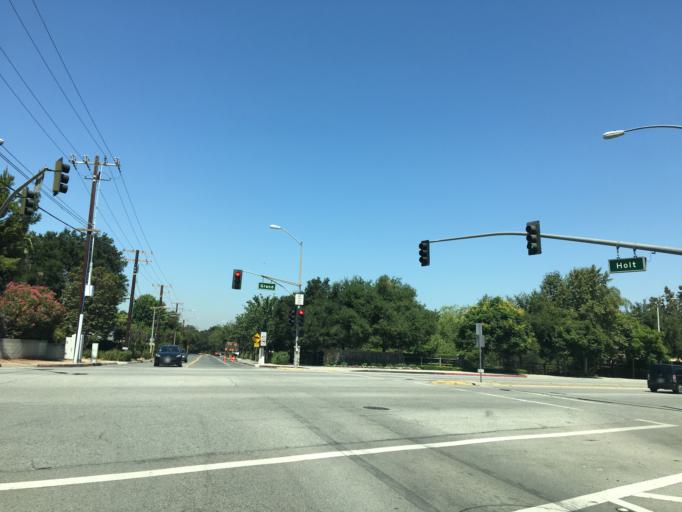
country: US
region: California
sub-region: Los Angeles County
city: Covina
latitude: 34.0691
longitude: -117.8719
